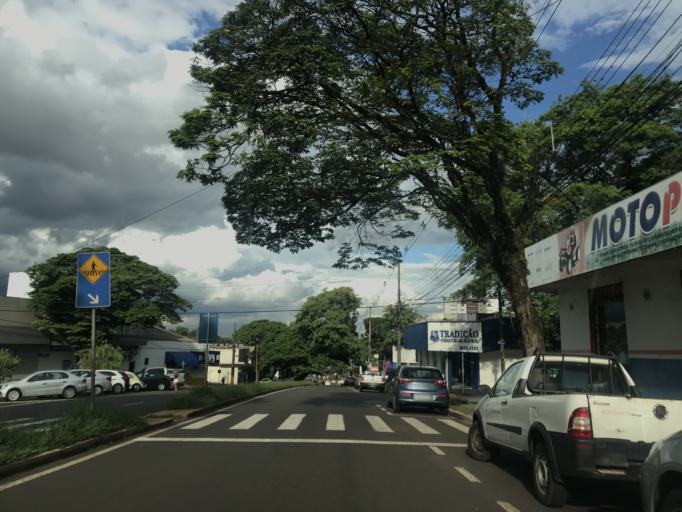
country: BR
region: Parana
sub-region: Maringa
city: Maringa
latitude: -23.4257
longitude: -51.9623
